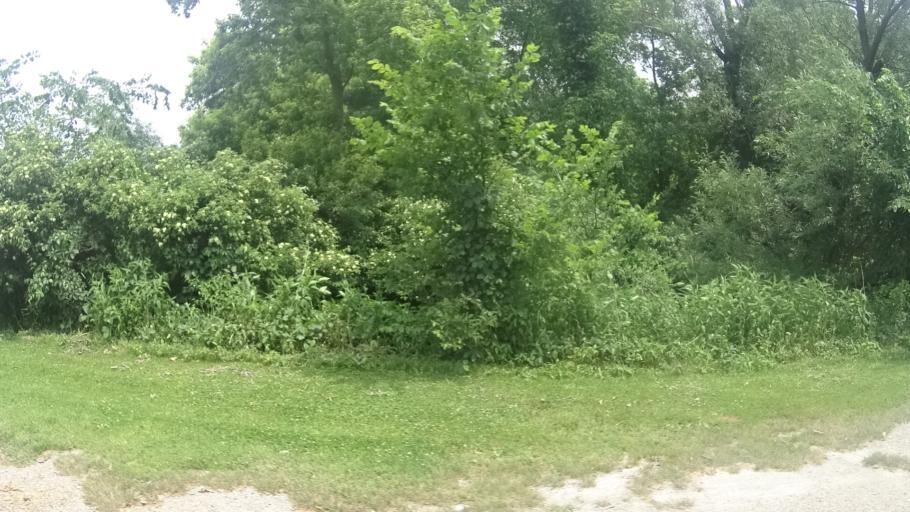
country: US
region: Ohio
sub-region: Erie County
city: Milan
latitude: 41.2967
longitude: -82.6427
